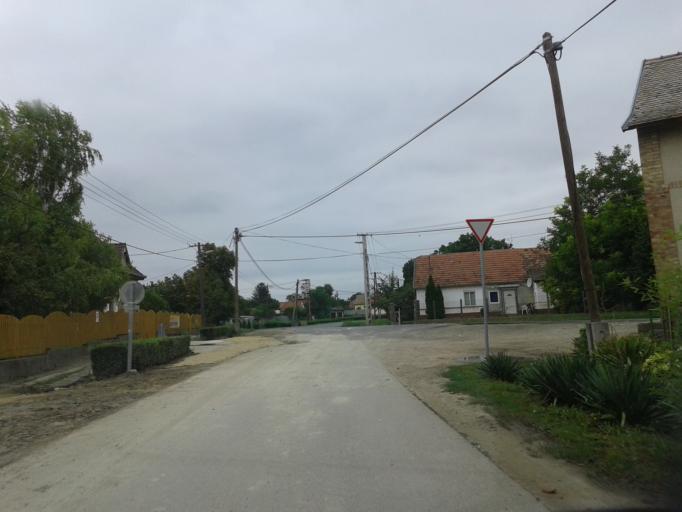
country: HU
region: Bacs-Kiskun
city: Szalkszentmarton
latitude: 46.9719
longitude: 19.0141
